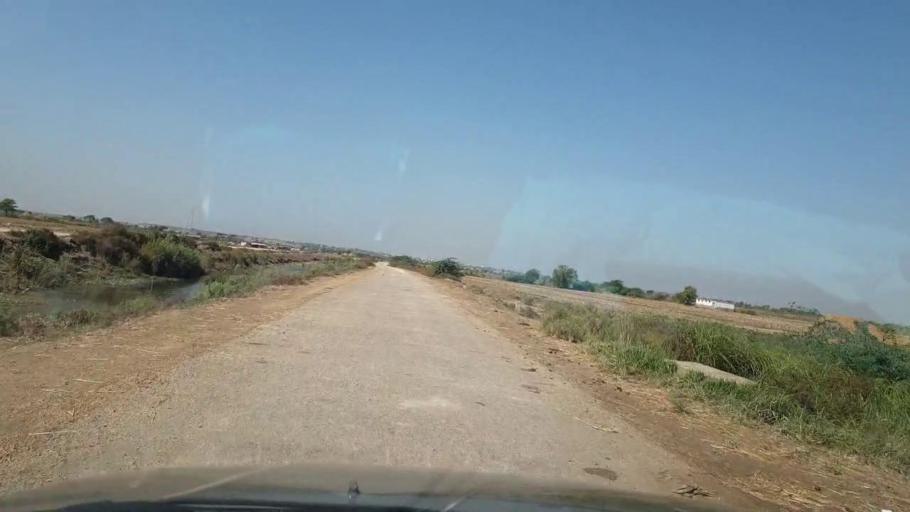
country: PK
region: Sindh
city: Thatta
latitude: 24.7232
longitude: 67.9289
